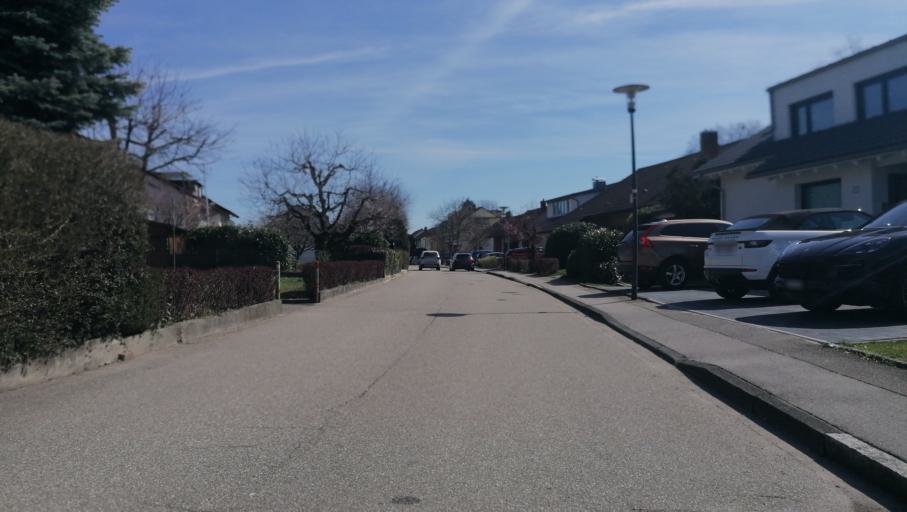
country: DE
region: Baden-Wuerttemberg
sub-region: Freiburg Region
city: Bad Sackingen
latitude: 47.5598
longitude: 7.9314
